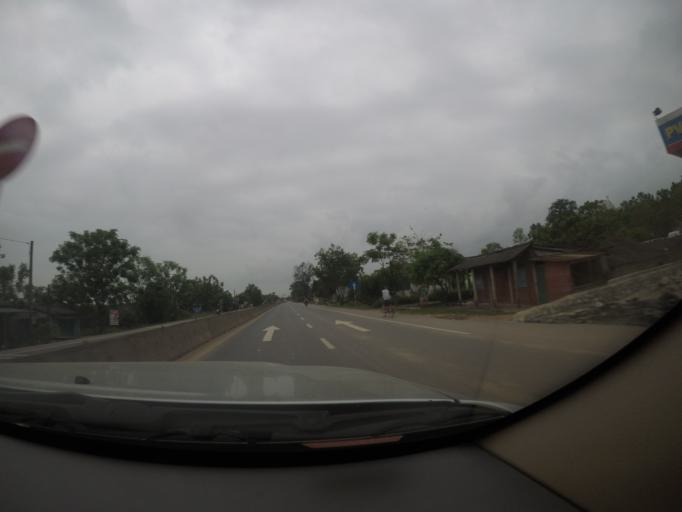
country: VN
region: Thua Thien-Hue
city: Phong Dien
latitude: 16.6073
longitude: 107.3220
